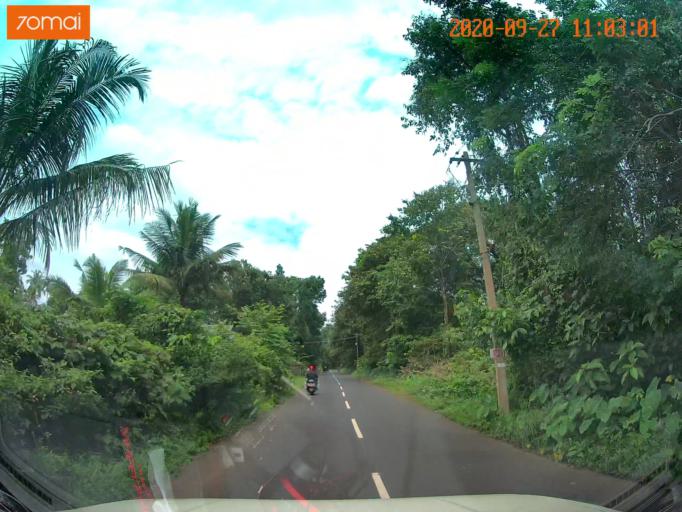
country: IN
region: Kerala
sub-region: Thrissur District
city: Irinjalakuda
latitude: 10.4201
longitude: 76.2606
